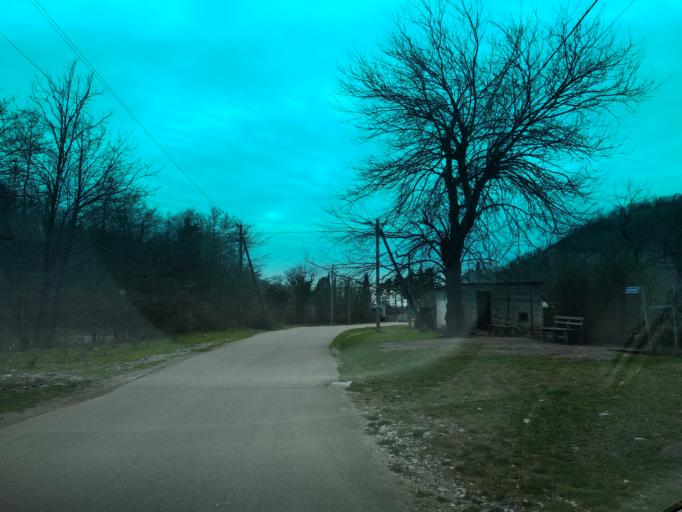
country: RU
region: Krasnodarskiy
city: Shepsi
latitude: 44.0606
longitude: 39.1361
